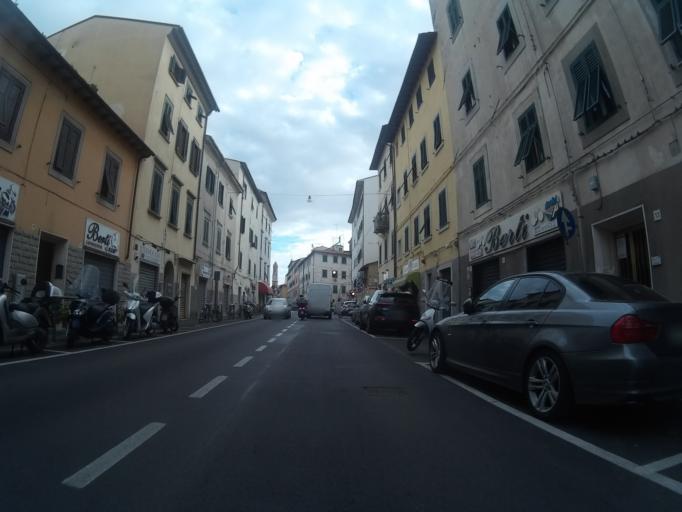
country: IT
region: Tuscany
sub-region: Provincia di Livorno
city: Livorno
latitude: 43.5571
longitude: 10.3166
